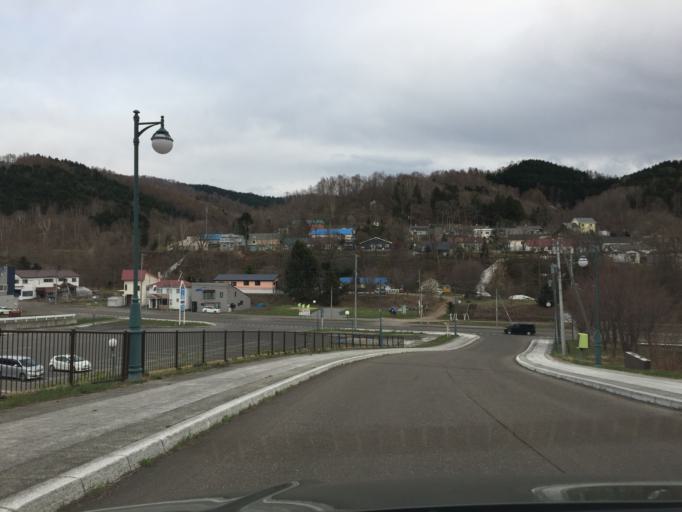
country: JP
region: Hokkaido
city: Utashinai
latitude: 43.5033
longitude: 142.0054
